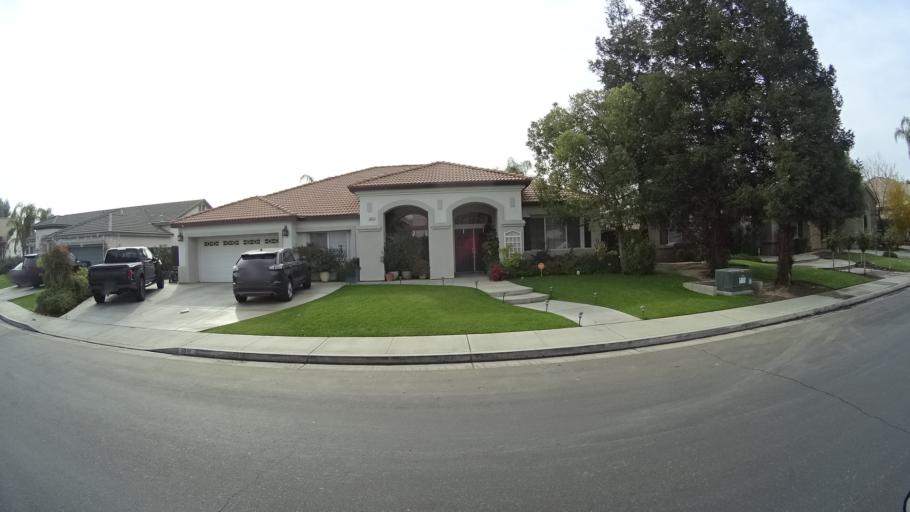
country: US
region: California
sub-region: Kern County
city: Rosedale
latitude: 35.3458
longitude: -119.1363
